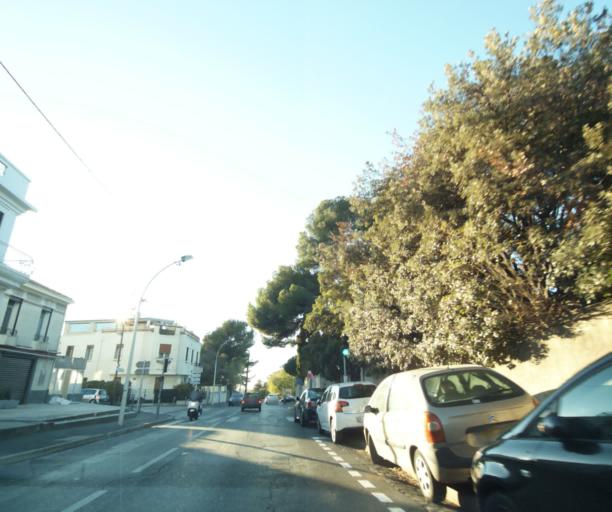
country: FR
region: Provence-Alpes-Cote d'Azur
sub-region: Departement des Bouches-du-Rhone
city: Marseille 12
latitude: 43.3080
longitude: 5.4325
